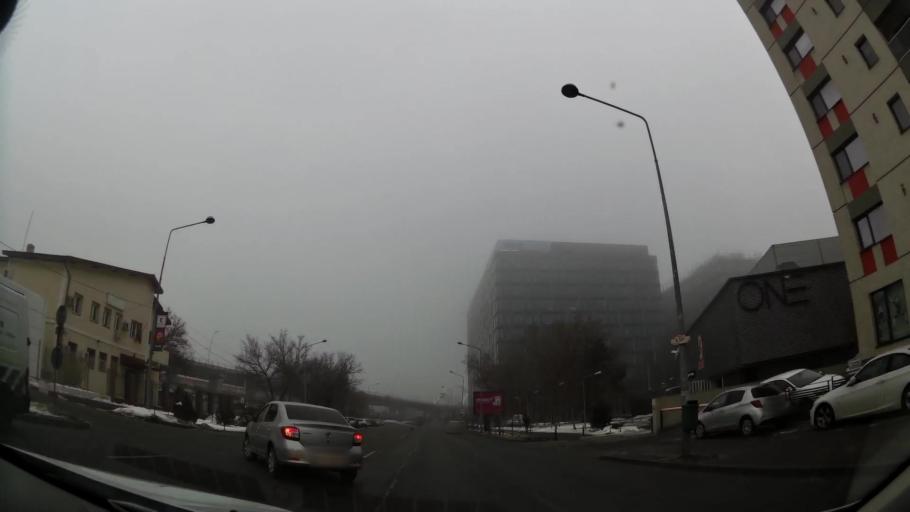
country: RO
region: Bucuresti
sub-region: Municipiul Bucuresti
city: Bucuresti
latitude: 44.4464
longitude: 26.0604
